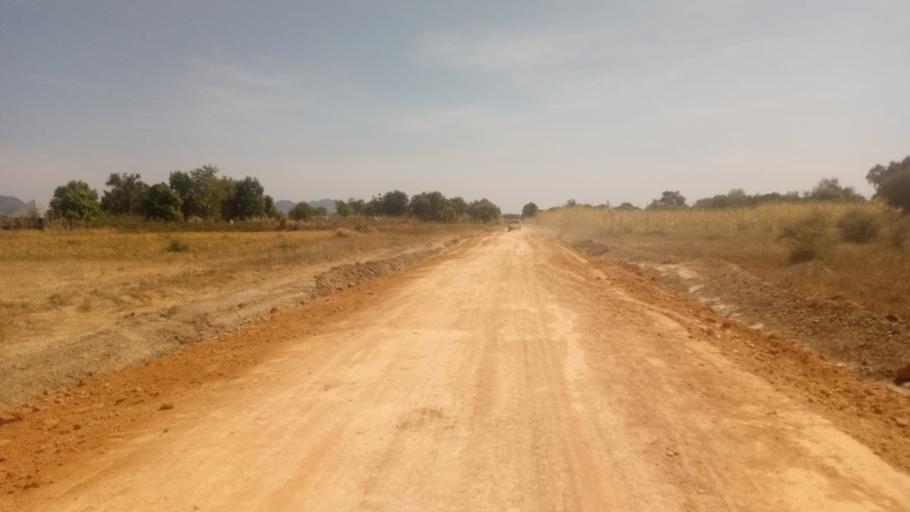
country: NG
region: Adamawa
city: Madagali
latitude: 10.8443
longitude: 13.3955
